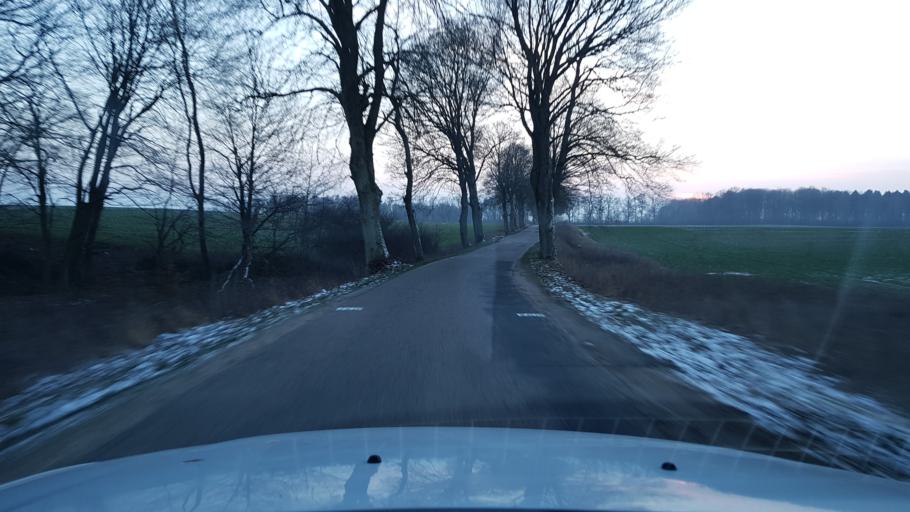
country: PL
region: West Pomeranian Voivodeship
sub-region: Powiat bialogardzki
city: Karlino
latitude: 54.0202
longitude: 15.8521
